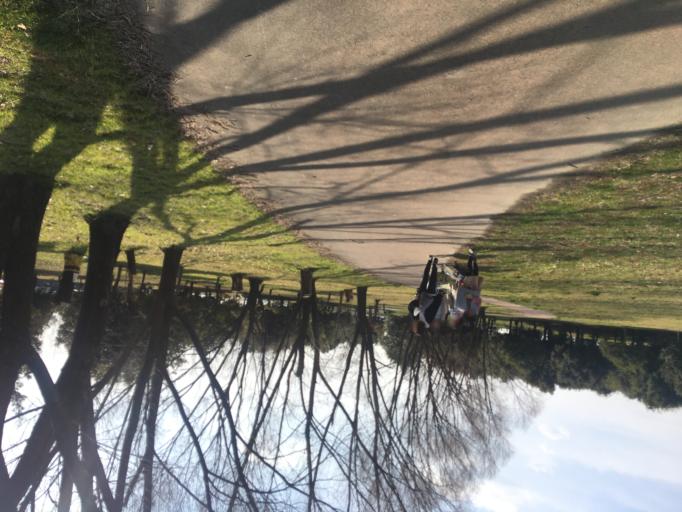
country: JP
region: Saitama
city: Kamifukuoka
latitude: 35.8770
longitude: 139.5565
